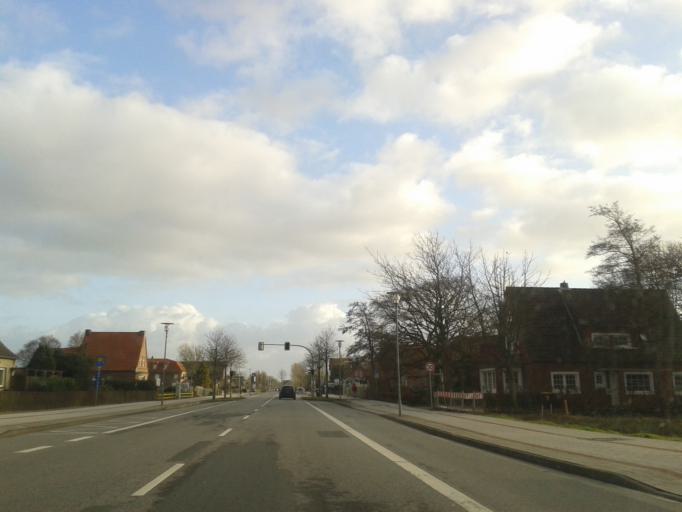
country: DE
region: Lower Saxony
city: Norddeich
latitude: 53.6154
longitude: 7.1636
